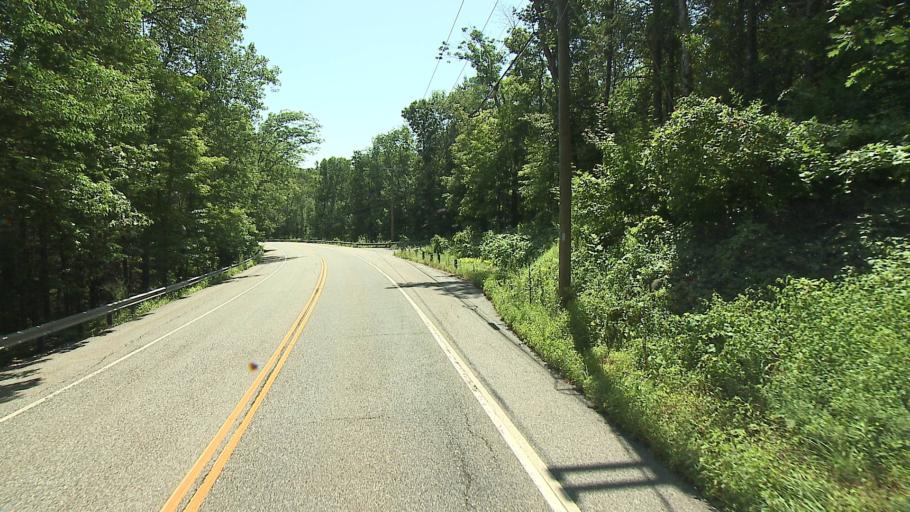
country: US
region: Connecticut
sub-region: Litchfield County
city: Kent
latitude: 41.8218
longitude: -73.3842
